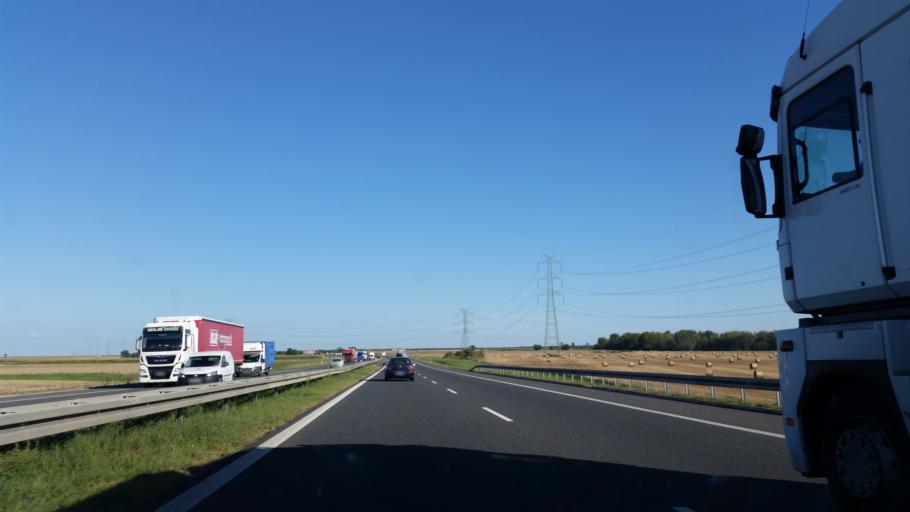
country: PL
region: Opole Voivodeship
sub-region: Powiat brzeski
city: Olszanka
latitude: 50.7467
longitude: 17.4491
